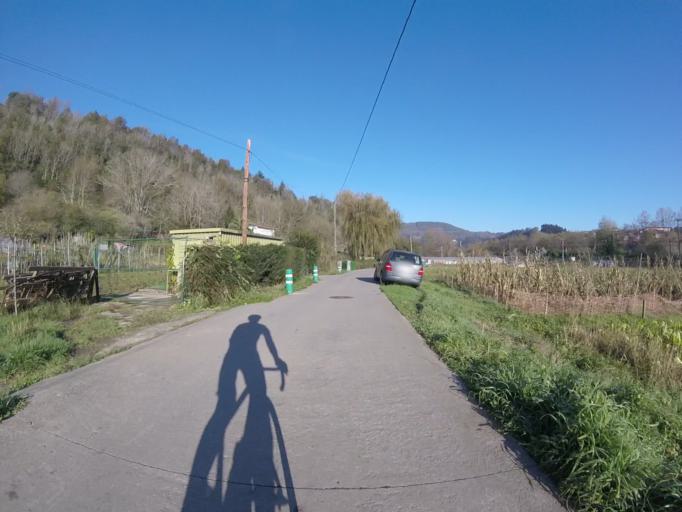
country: ES
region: Basque Country
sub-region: Provincia de Guipuzcoa
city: Usurbil
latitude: 43.2684
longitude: -2.0572
